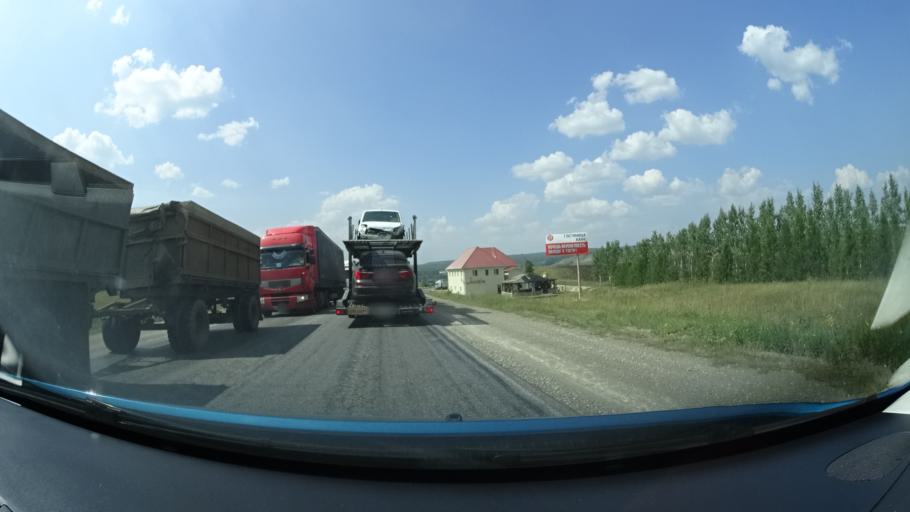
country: RU
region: Bashkortostan
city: Serafimovskiy
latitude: 54.4561
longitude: 53.6857
